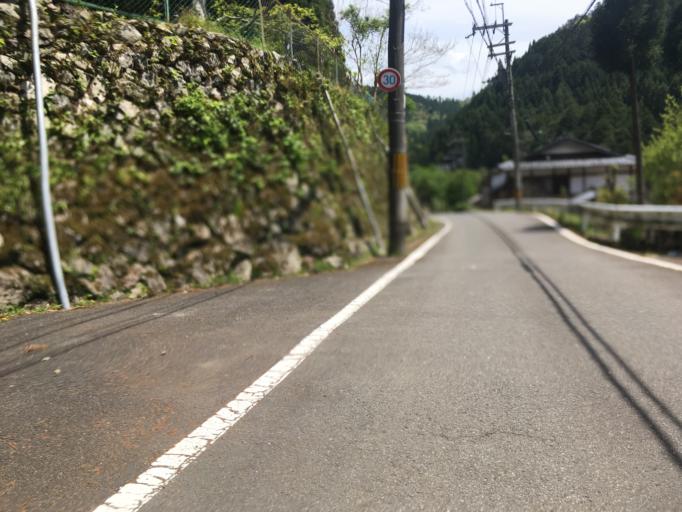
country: JP
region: Kyoto
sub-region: Kyoto-shi
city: Kamigyo-ku
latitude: 35.1137
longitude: 135.7186
